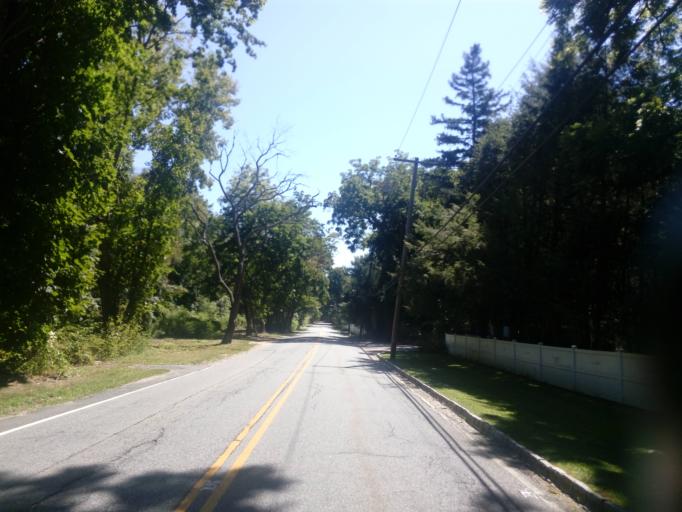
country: US
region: New York
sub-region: Nassau County
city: Upper Brookville
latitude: 40.8435
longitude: -73.5730
